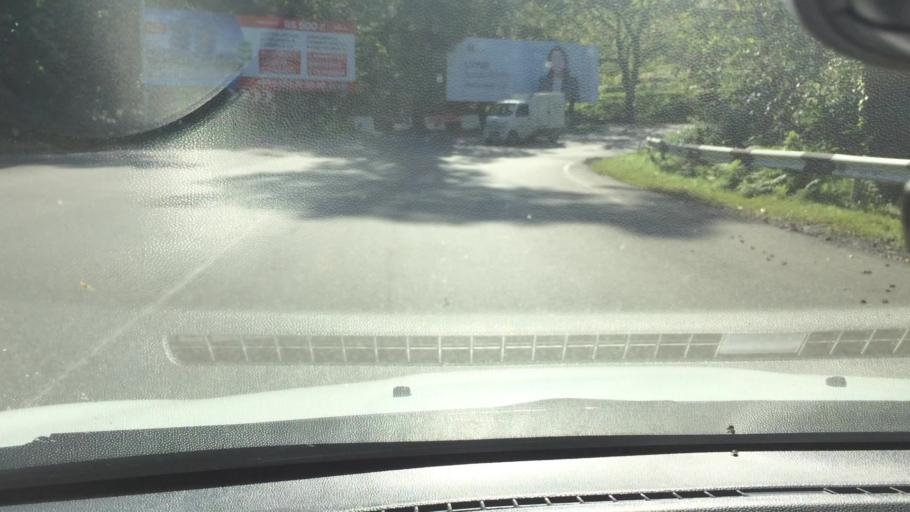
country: GE
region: Ajaria
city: Kobuleti
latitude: 41.7649
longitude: 41.7551
